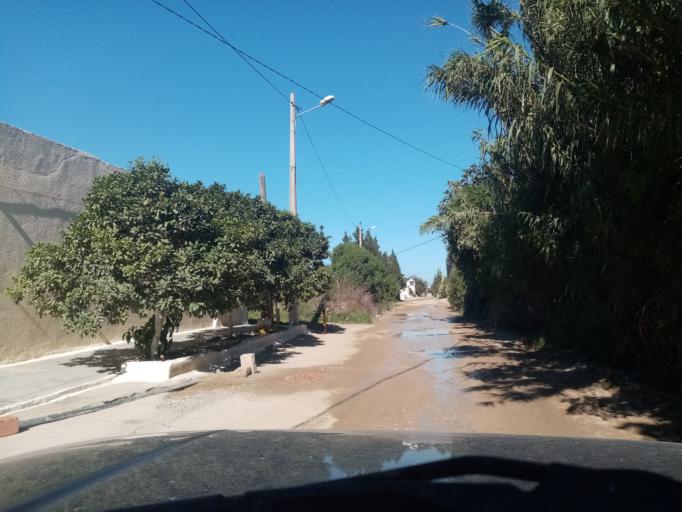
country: TN
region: Nabul
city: Bu `Urqub
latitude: 36.5750
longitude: 10.5728
